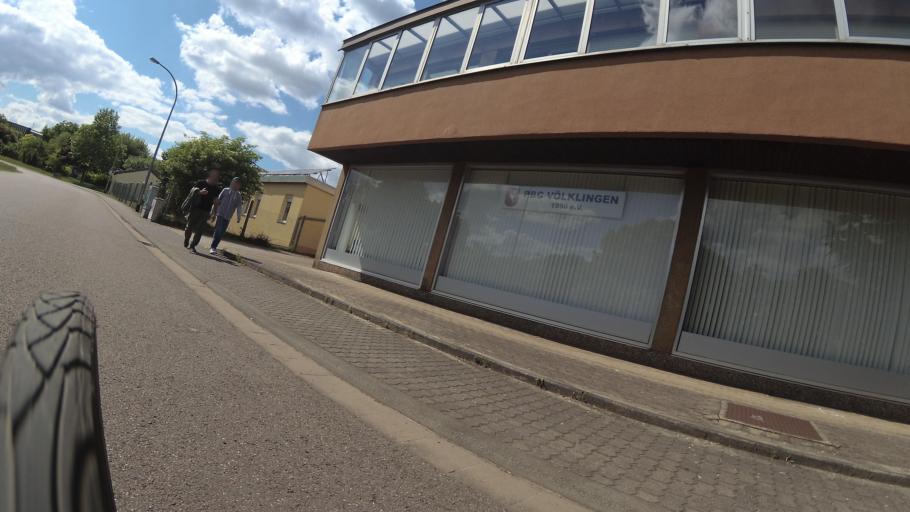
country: DE
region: Saarland
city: Volklingen
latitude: 49.2600
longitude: 6.8613
